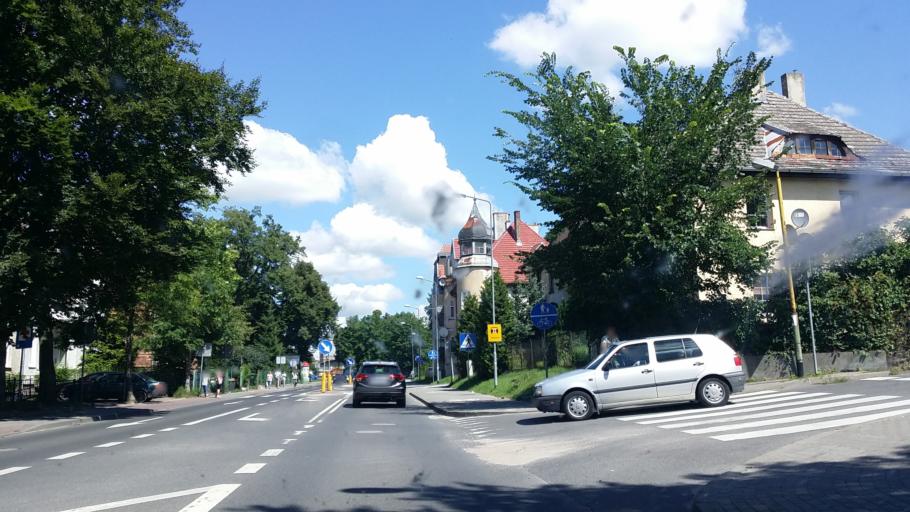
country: PL
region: West Pomeranian Voivodeship
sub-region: Powiat swidwinski
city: Swidwin
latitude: 53.7680
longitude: 15.7735
